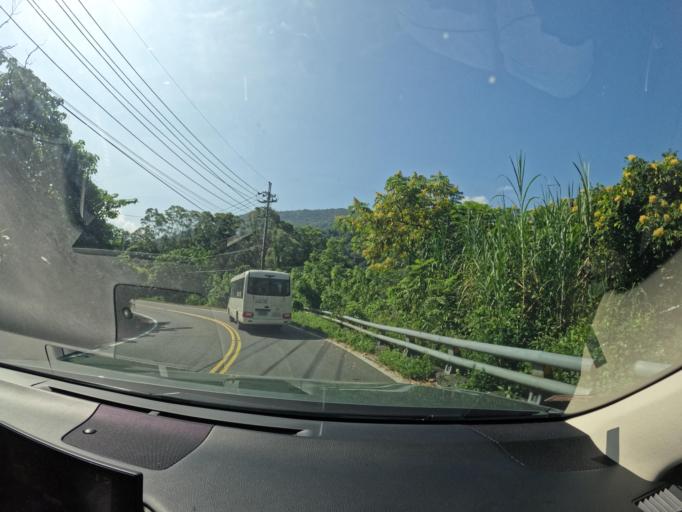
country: TW
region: Taiwan
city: Yujing
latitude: 23.0697
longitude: 120.6462
